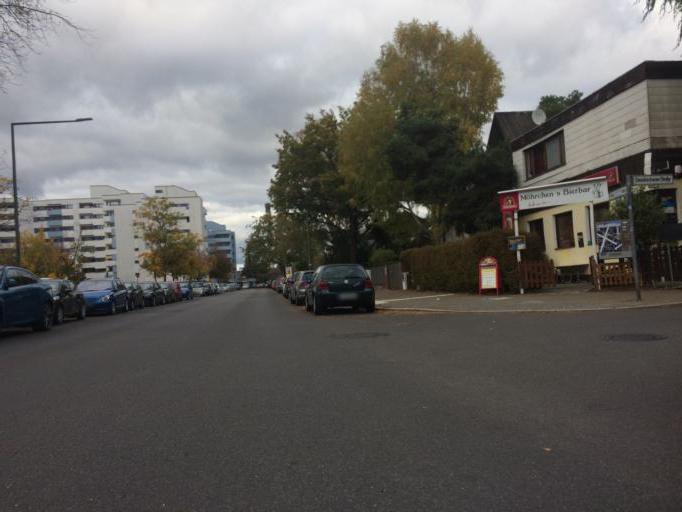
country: DE
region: Berlin
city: Wittenau
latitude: 52.5965
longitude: 13.3393
